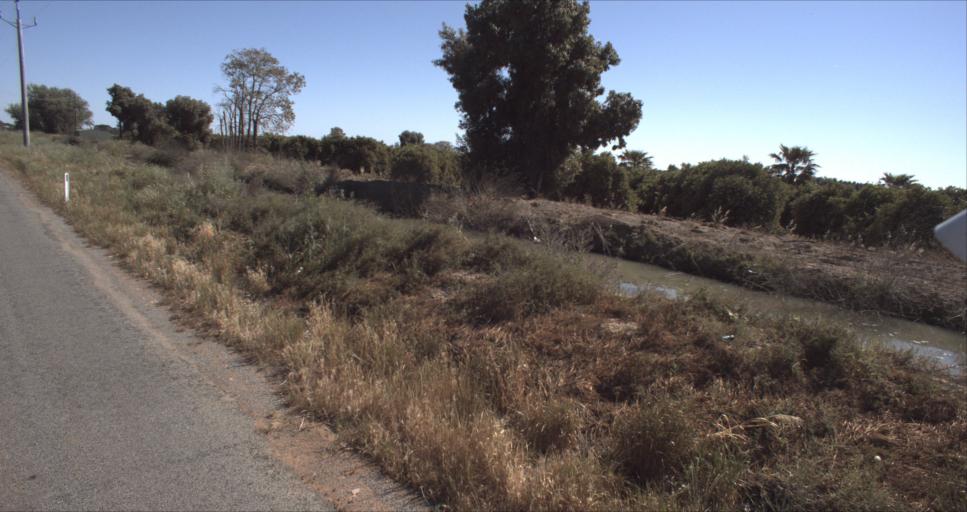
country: AU
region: New South Wales
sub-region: Leeton
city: Leeton
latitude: -34.5432
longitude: 146.3436
